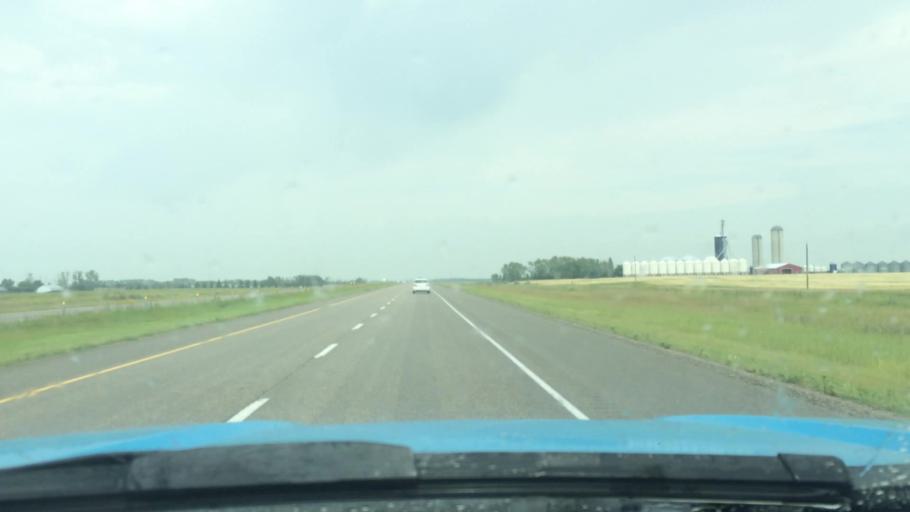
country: CA
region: Alberta
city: Olds
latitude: 51.7155
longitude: -114.0254
